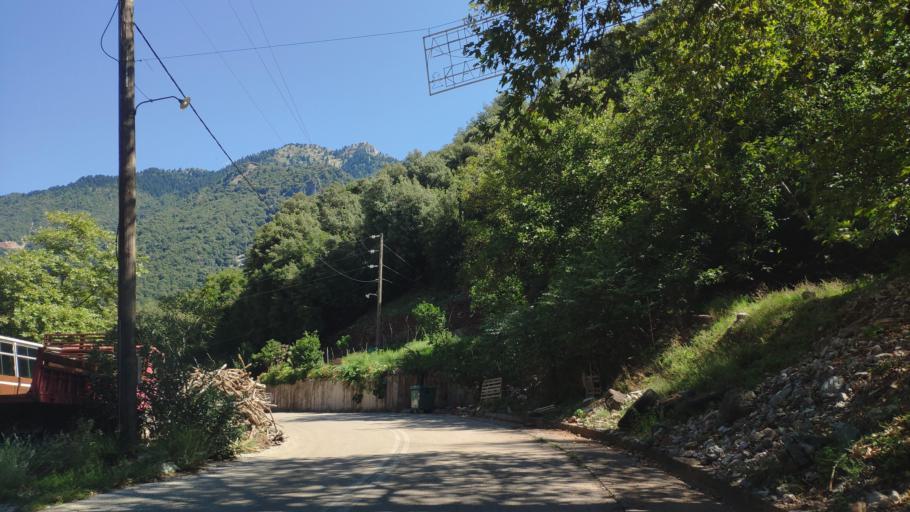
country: GR
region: Central Greece
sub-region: Nomos Evrytanias
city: Kerasochori
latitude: 39.0539
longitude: 21.6042
